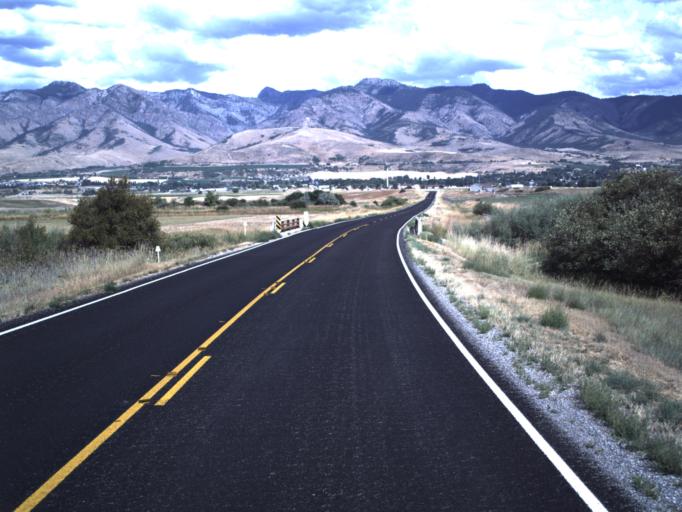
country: US
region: Utah
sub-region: Cache County
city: Richmond
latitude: 41.9250
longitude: -111.8520
